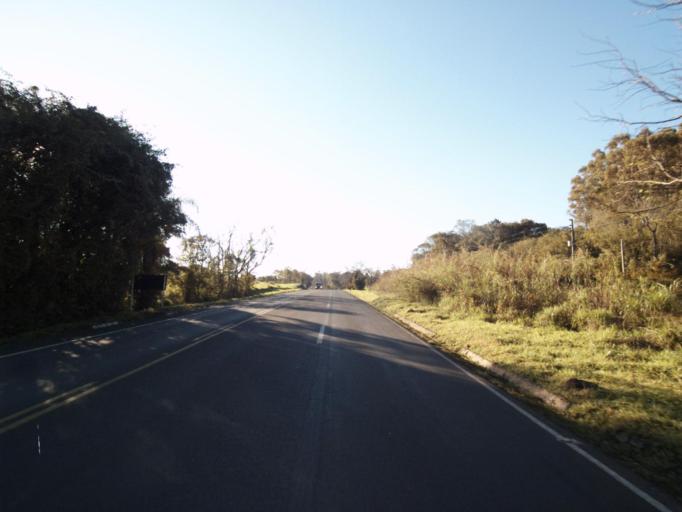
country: BR
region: Santa Catarina
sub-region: Chapeco
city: Chapeco
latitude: -26.9051
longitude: -52.8676
